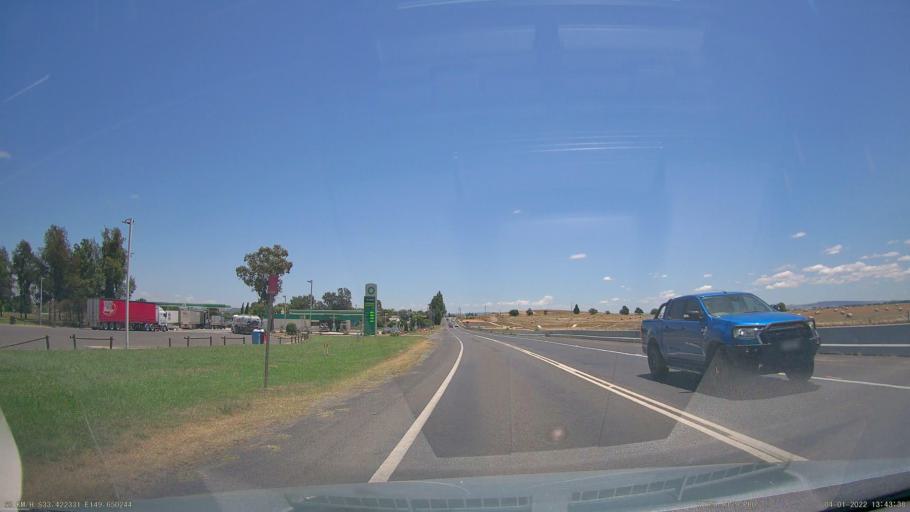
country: AU
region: New South Wales
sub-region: Bathurst Regional
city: Kelso
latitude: -33.4228
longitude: 149.6498
